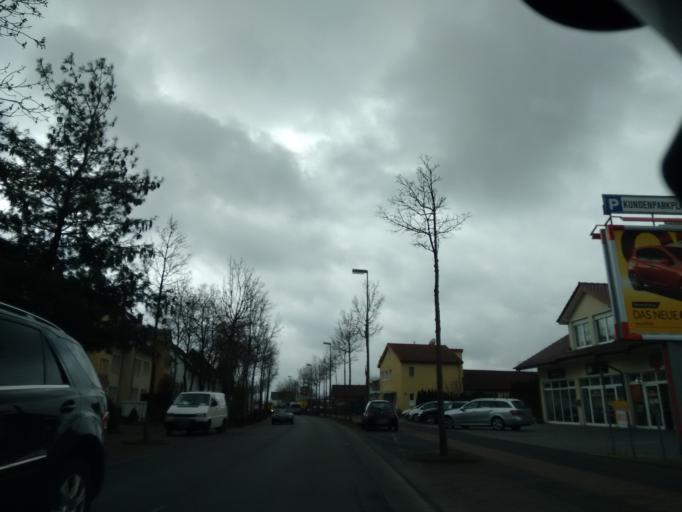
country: DE
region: North Rhine-Westphalia
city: Bad Lippspringe
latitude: 51.7768
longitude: 8.8068
